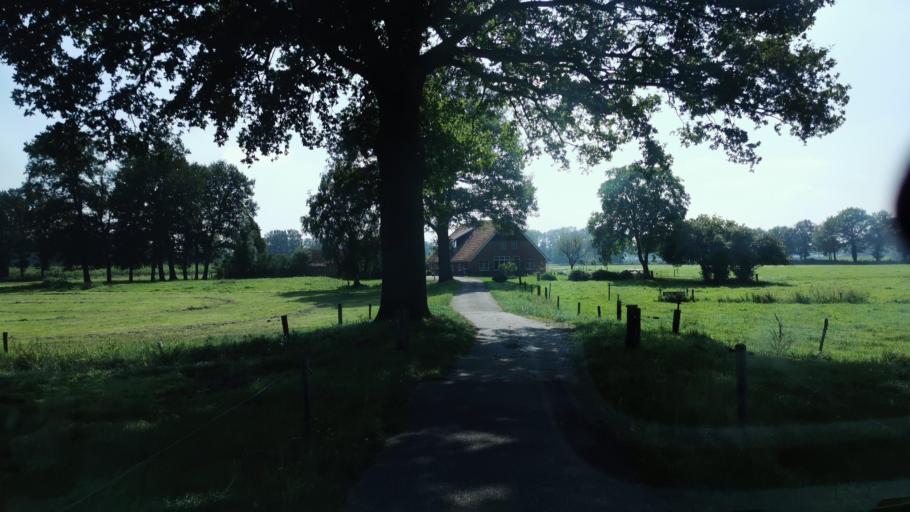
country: NL
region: Overijssel
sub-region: Gemeente Oldenzaal
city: Oldenzaal
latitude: 52.3524
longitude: 6.8868
